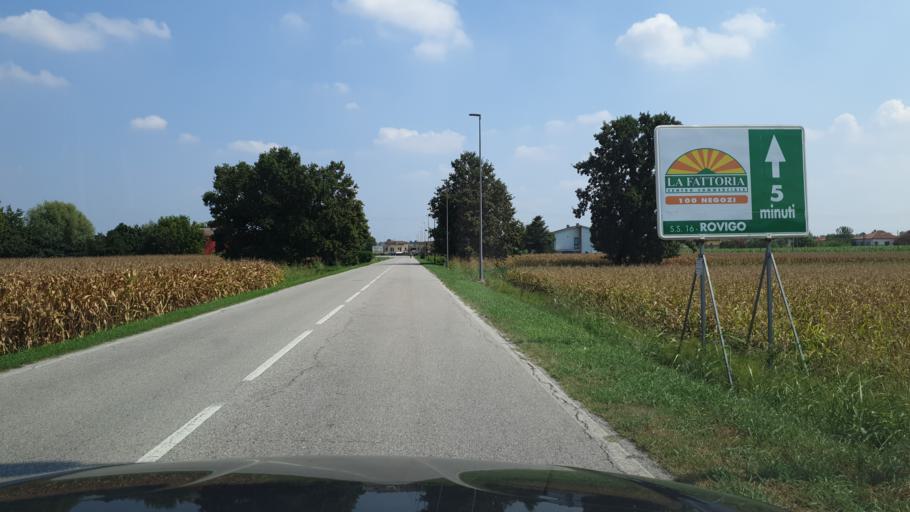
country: IT
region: Veneto
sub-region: Provincia di Rovigo
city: Arqua Polesine
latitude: 45.0130
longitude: 11.7307
